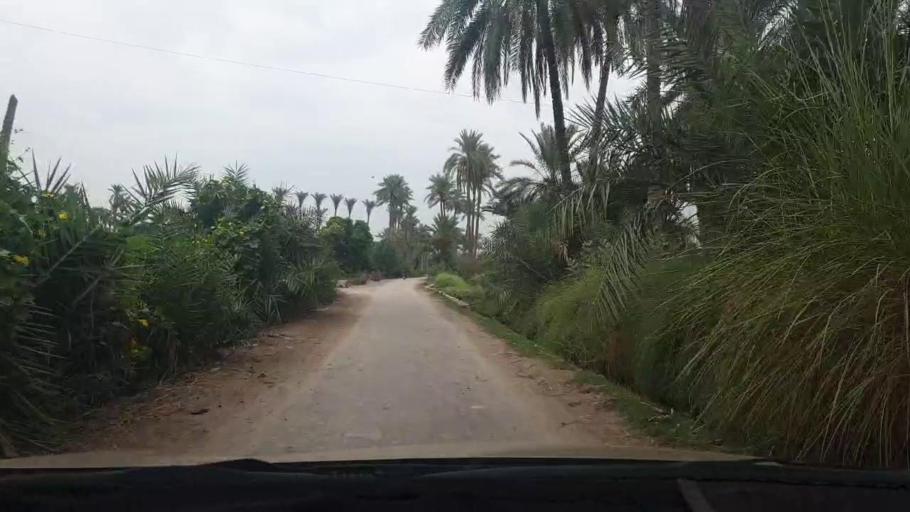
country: PK
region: Sindh
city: Larkana
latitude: 27.5629
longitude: 68.2308
